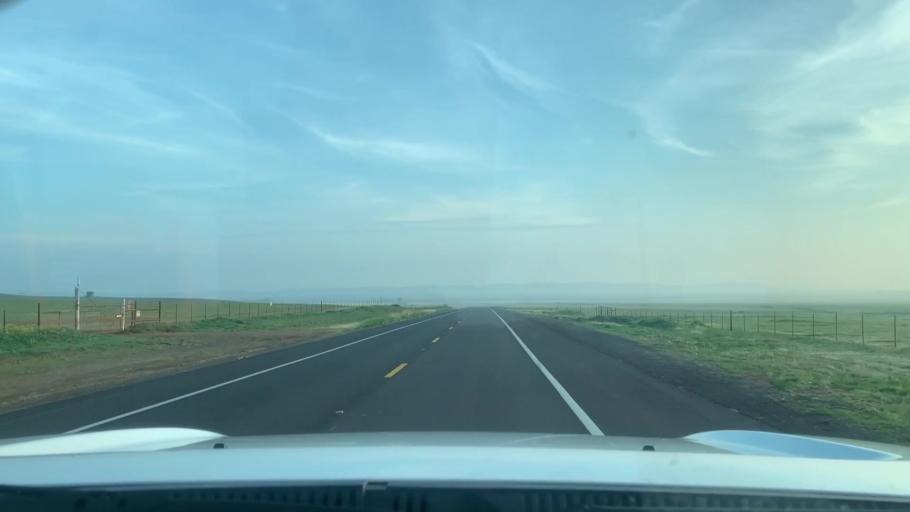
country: US
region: California
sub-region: Kings County
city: Avenal
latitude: 35.7822
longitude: -120.1232
